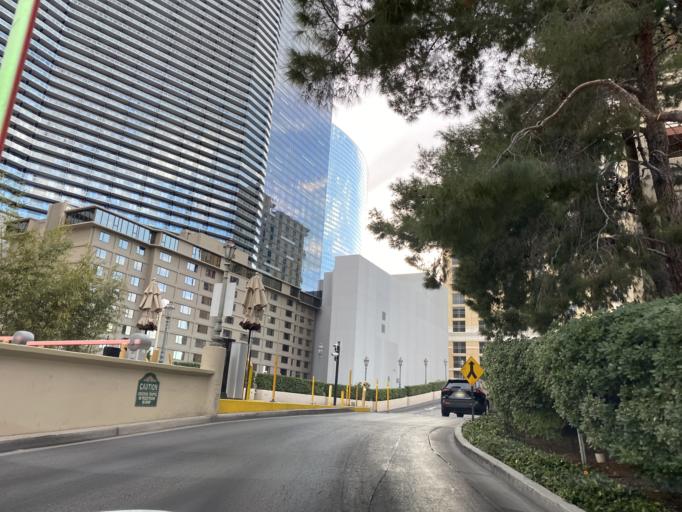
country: US
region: Nevada
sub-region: Clark County
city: Paradise
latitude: 36.1109
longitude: -115.1749
